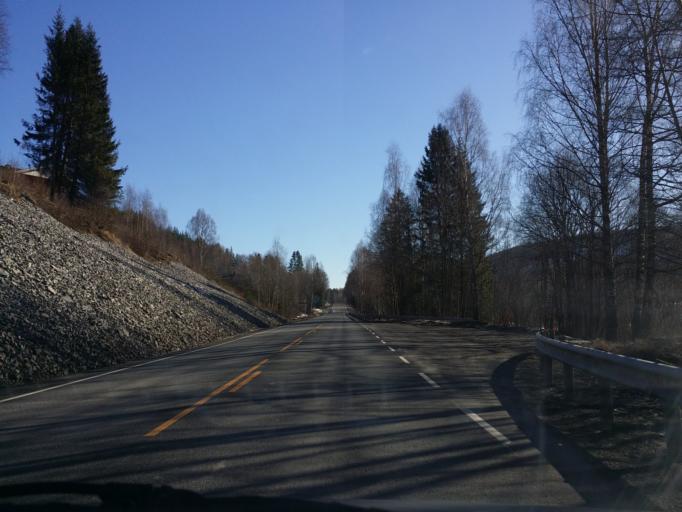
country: NO
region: Buskerud
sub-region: Ringerike
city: Honefoss
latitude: 60.3269
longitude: 10.1299
